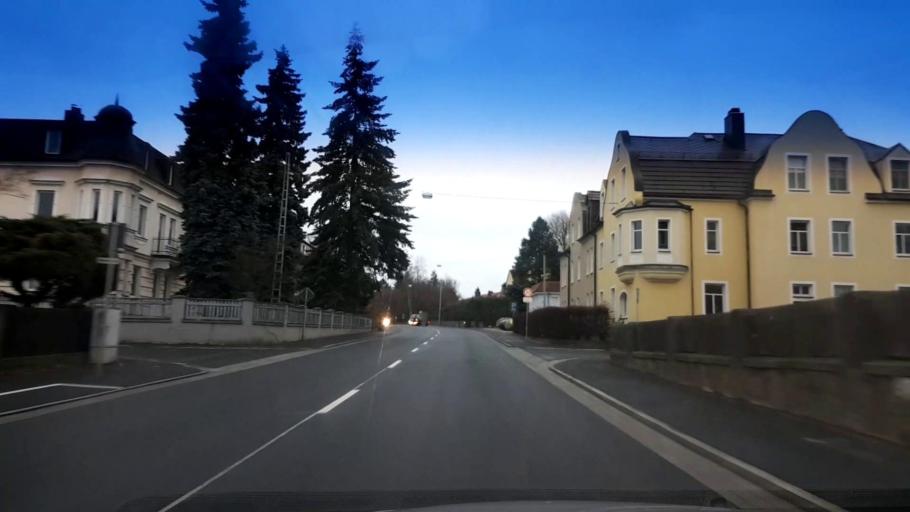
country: DE
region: Bavaria
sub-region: Upper Palatinate
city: Waldsassen
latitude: 49.9995
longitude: 12.2961
